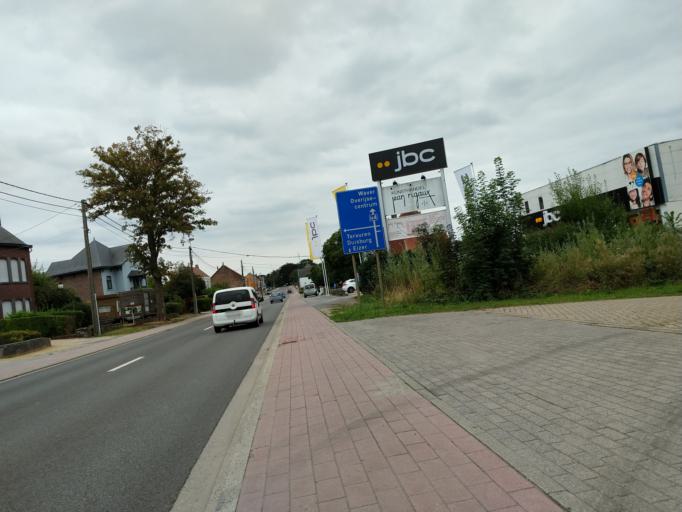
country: BE
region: Flanders
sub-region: Provincie Vlaams-Brabant
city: Overijse
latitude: 50.7796
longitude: 4.5179
